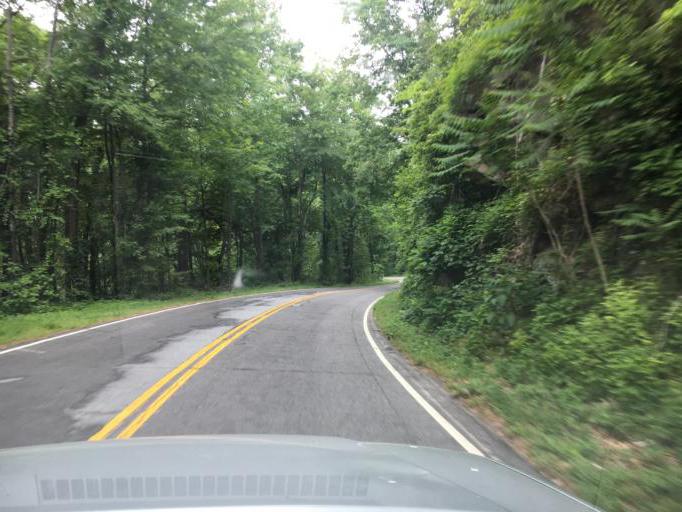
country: US
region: South Carolina
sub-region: Greenville County
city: Tigerville
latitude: 35.1641
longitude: -82.4082
